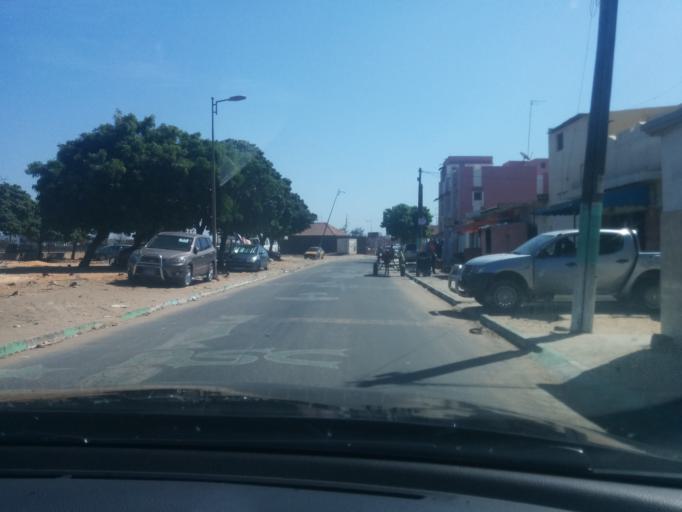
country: SN
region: Dakar
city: Grand Dakar
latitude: 14.7424
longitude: -17.4419
